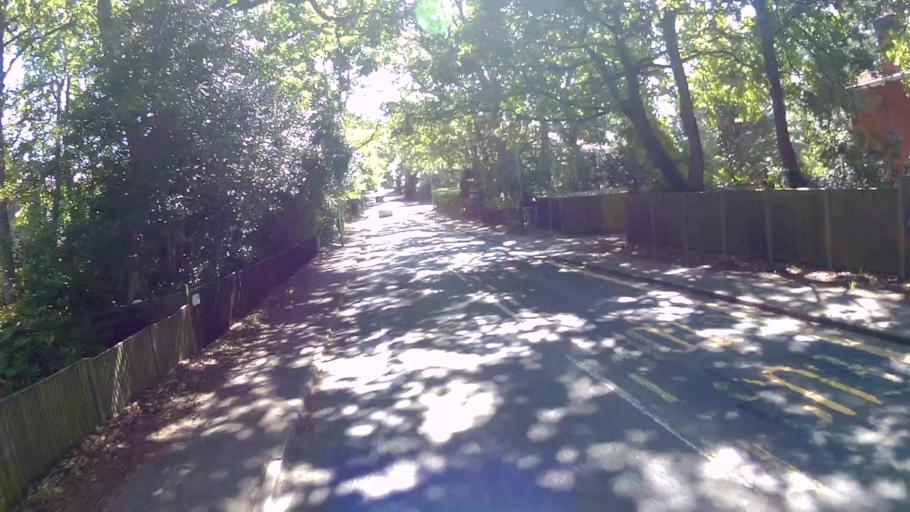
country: GB
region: England
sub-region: Hampshire
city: Yateley
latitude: 51.3707
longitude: -0.8245
